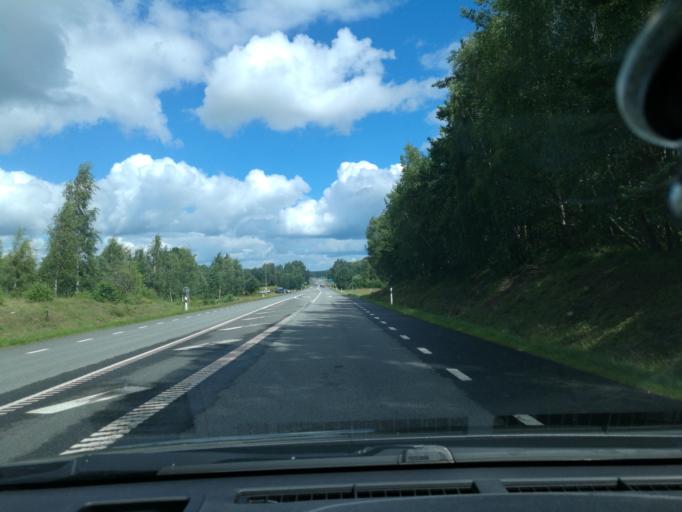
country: SE
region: Skane
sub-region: Hassleholms Kommun
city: Hassleholm
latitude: 56.1544
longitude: 13.8134
